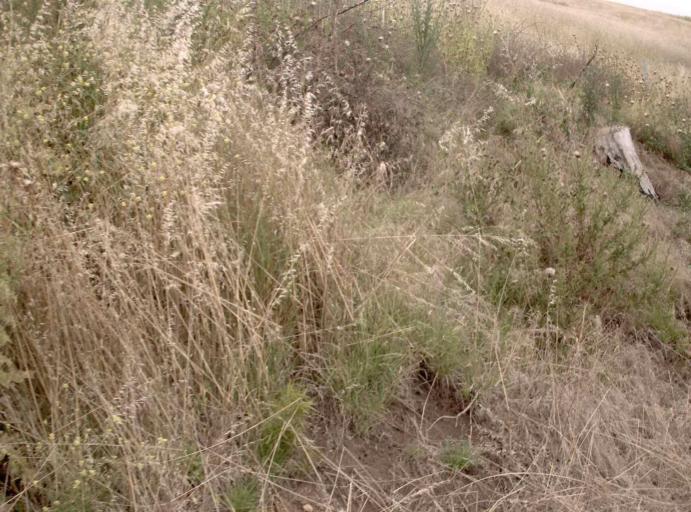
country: AU
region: Victoria
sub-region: Wellington
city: Heyfield
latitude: -37.8234
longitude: 146.6754
